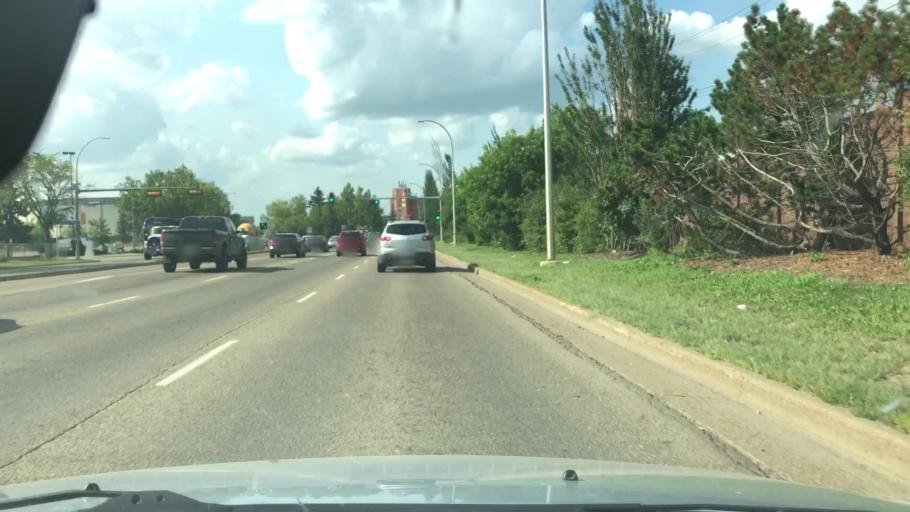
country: CA
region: Alberta
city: Edmonton
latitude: 53.5674
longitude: -113.4505
